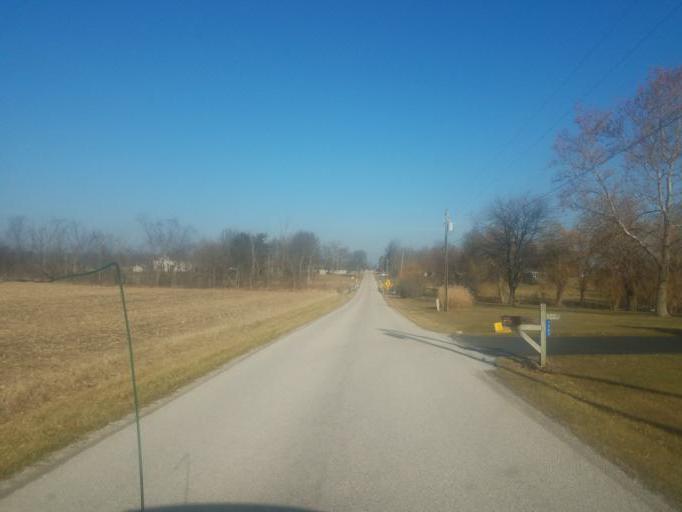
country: US
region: Ohio
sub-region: Seneca County
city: Tiffin
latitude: 41.1066
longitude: -83.1120
